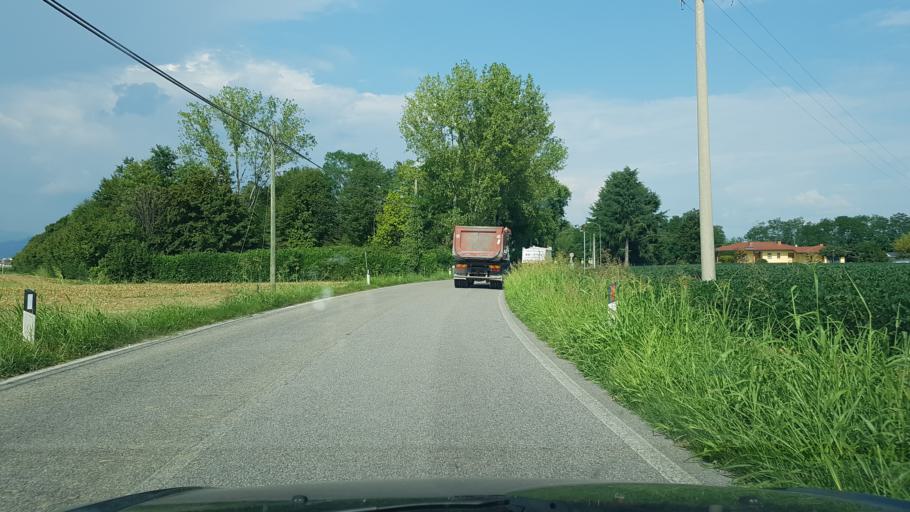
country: IT
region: Friuli Venezia Giulia
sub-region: Provincia di Pordenone
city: Spilimbergo
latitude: 46.0993
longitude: 12.8893
